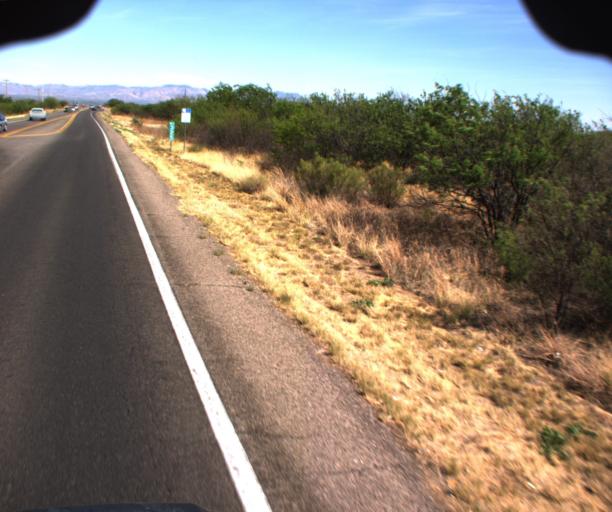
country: US
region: Arizona
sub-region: Cochise County
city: Sierra Vista Southeast
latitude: 31.5532
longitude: -110.1987
